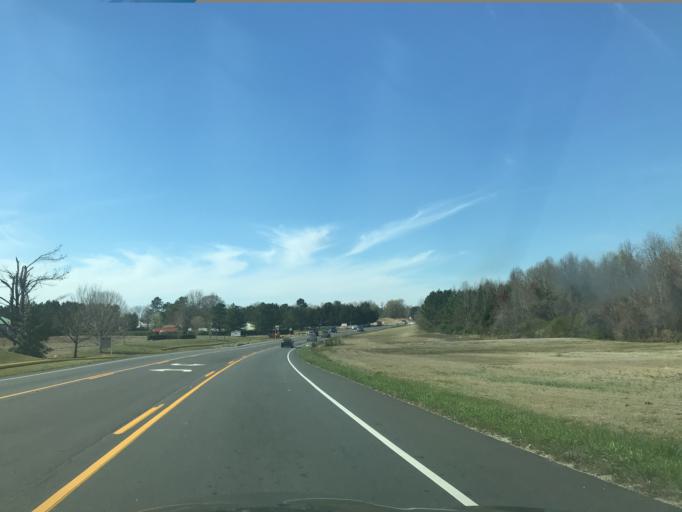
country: US
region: North Carolina
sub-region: Harnett County
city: Angier
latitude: 35.5460
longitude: -78.7539
